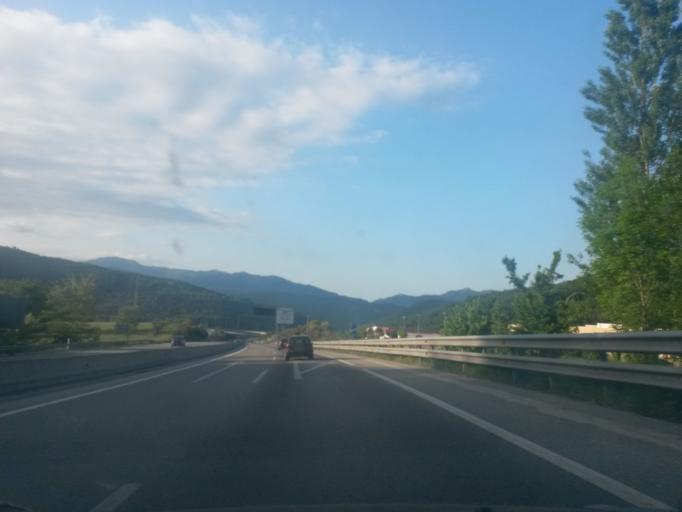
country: ES
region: Catalonia
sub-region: Provincia de Girona
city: Sant Joan les Fonts
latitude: 42.2041
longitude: 2.5377
